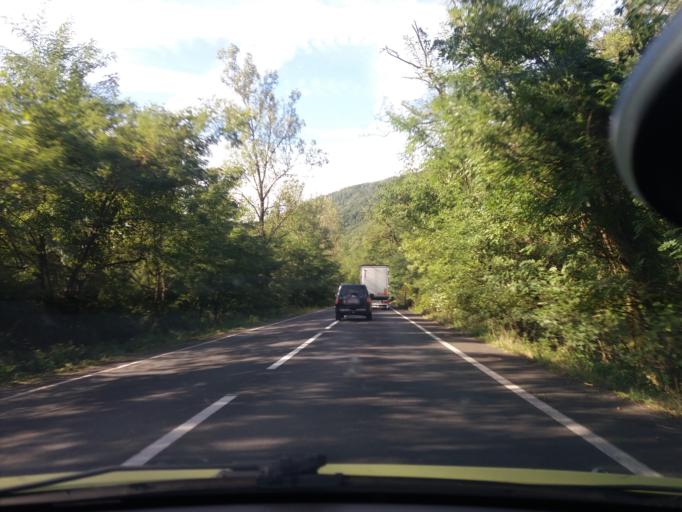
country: RO
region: Arad
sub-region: Comuna Savarsin
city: Savarsin
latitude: 46.0061
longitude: 22.2748
